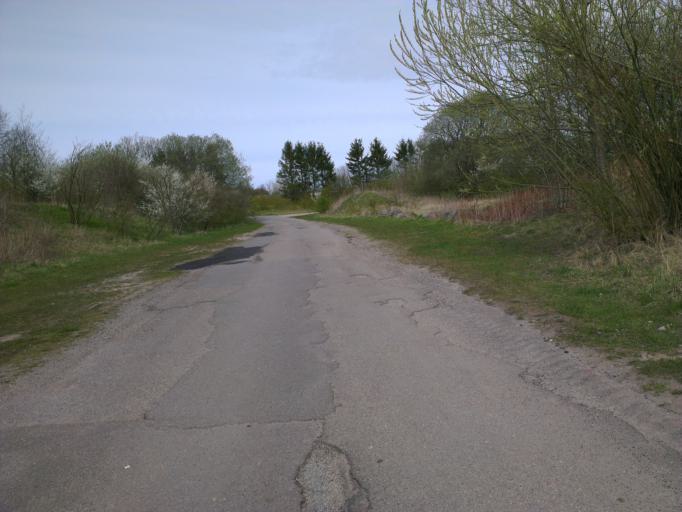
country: DK
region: Capital Region
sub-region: Frederikssund Kommune
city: Frederikssund
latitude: 55.8347
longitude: 12.0902
